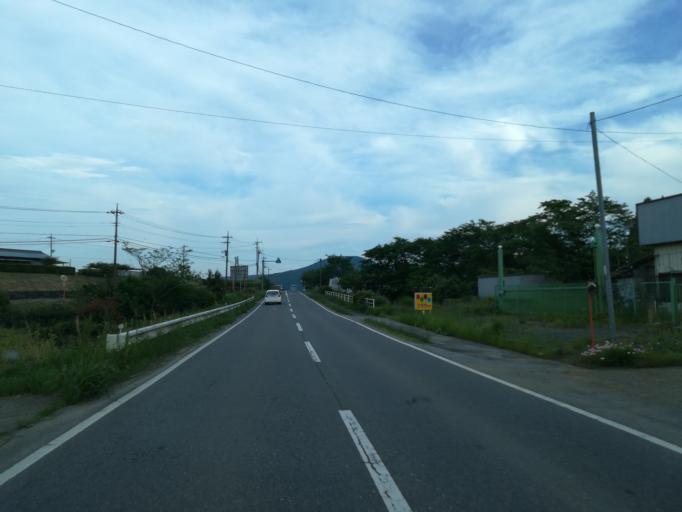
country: JP
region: Ibaraki
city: Tsukuba
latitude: 36.2157
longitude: 140.1707
